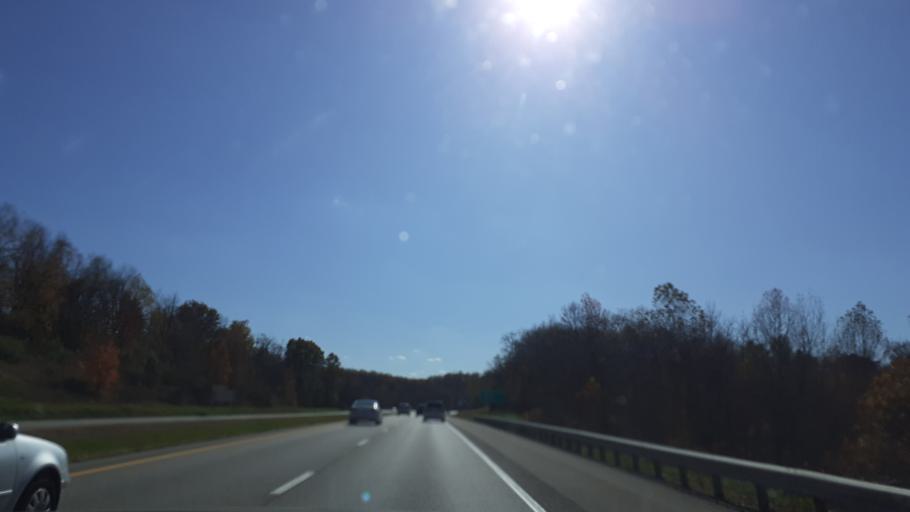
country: US
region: West Virginia
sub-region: Monongalia County
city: Brookhaven
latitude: 39.6333
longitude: -79.9002
